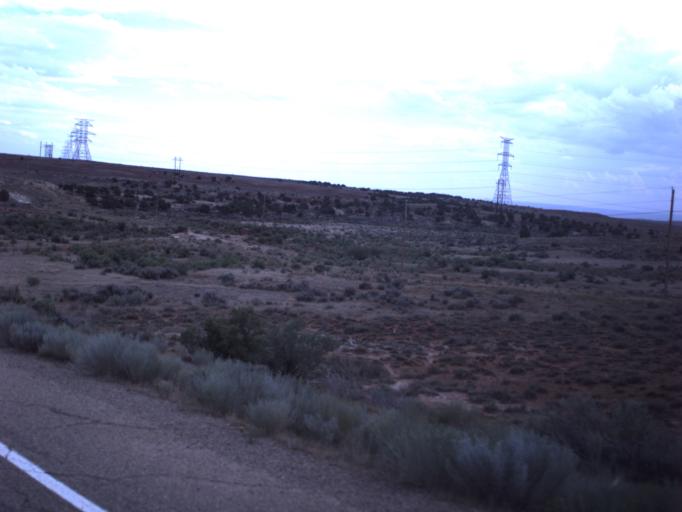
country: US
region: Utah
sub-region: Uintah County
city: Naples
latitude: 40.1665
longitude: -109.3152
